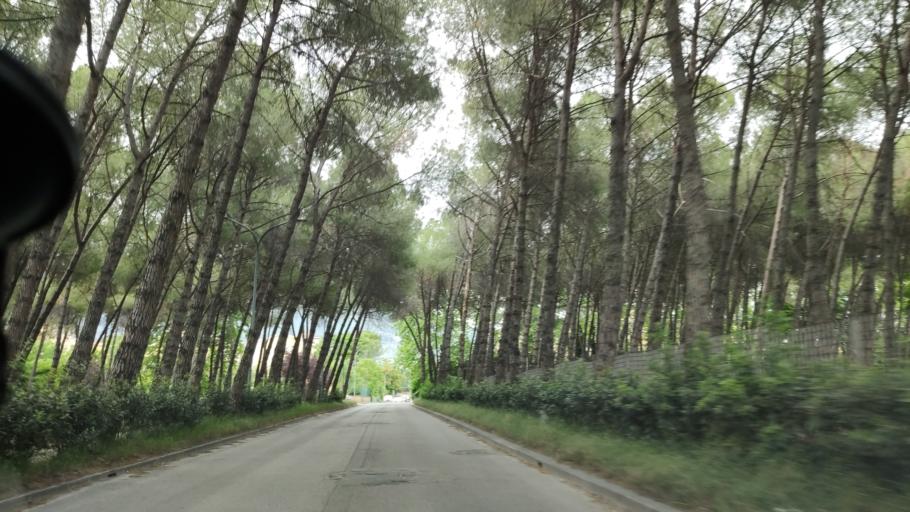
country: IT
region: Umbria
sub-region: Provincia di Terni
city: Terni
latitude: 42.5616
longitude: 12.6580
